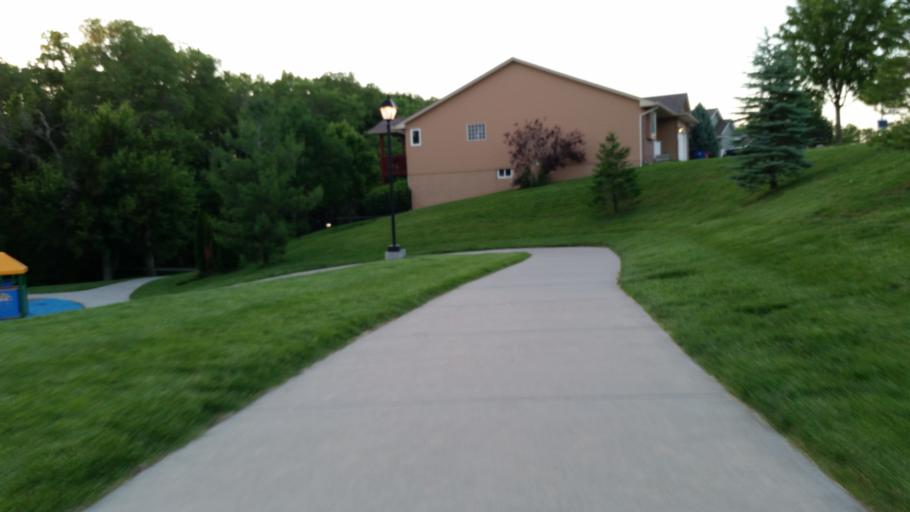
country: US
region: Nebraska
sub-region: Sarpy County
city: Offutt Air Force Base
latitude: 41.1074
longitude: -95.9552
